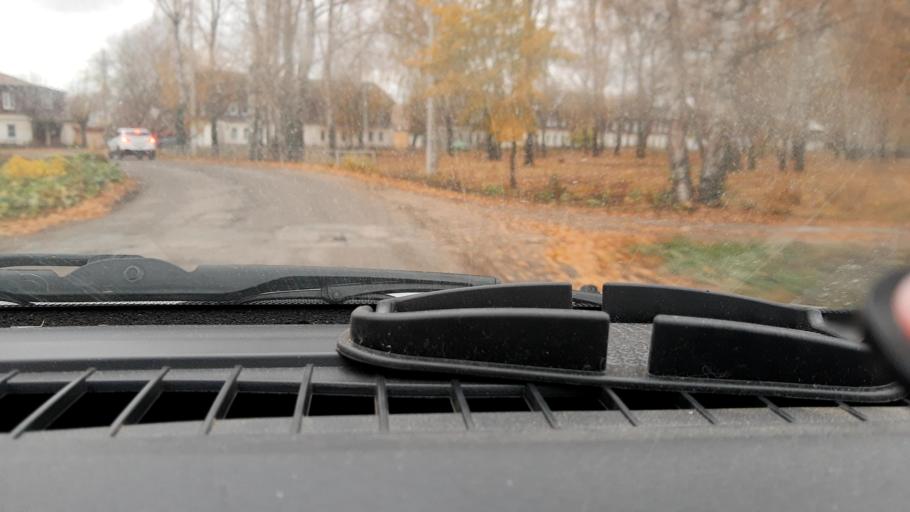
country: RU
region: Nizjnij Novgorod
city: Neklyudovo
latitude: 56.4091
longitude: 44.0331
